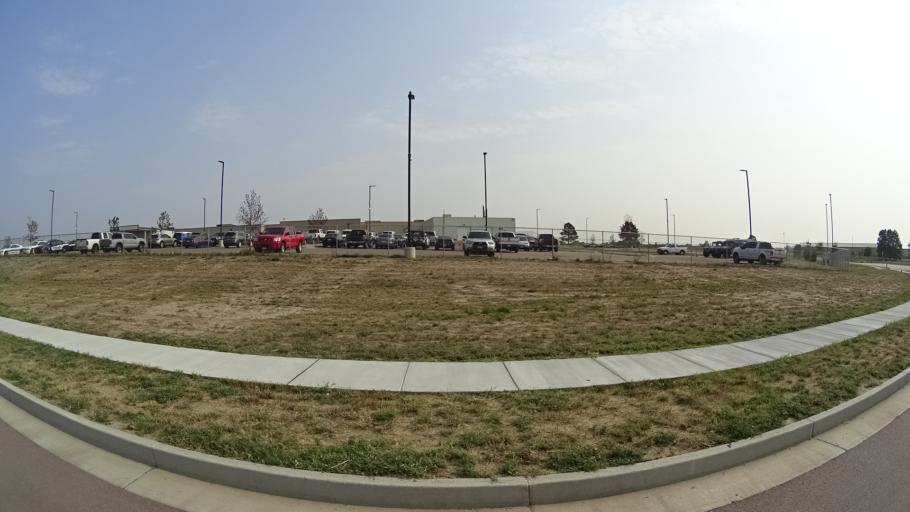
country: US
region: Colorado
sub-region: El Paso County
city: Stratmoor
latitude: 38.8150
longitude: -104.7548
